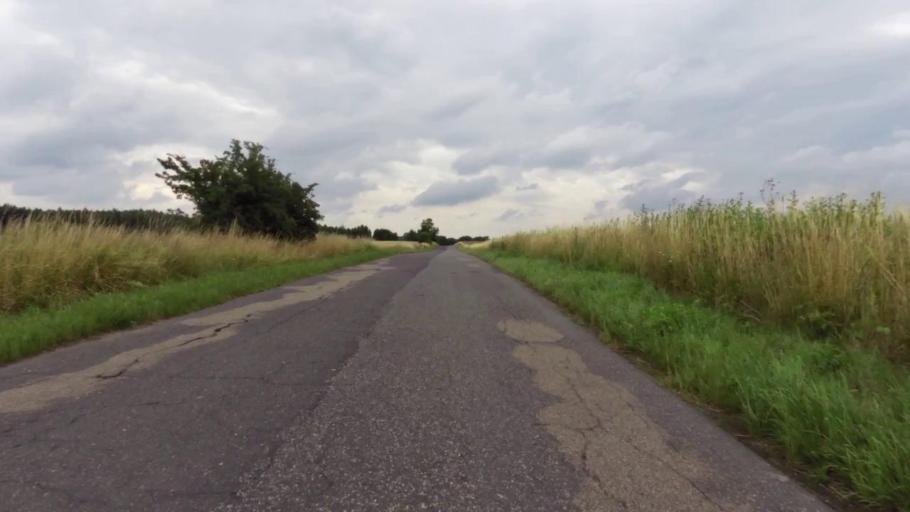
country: PL
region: West Pomeranian Voivodeship
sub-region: Powiat mysliborski
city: Mysliborz
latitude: 52.9568
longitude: 14.8817
